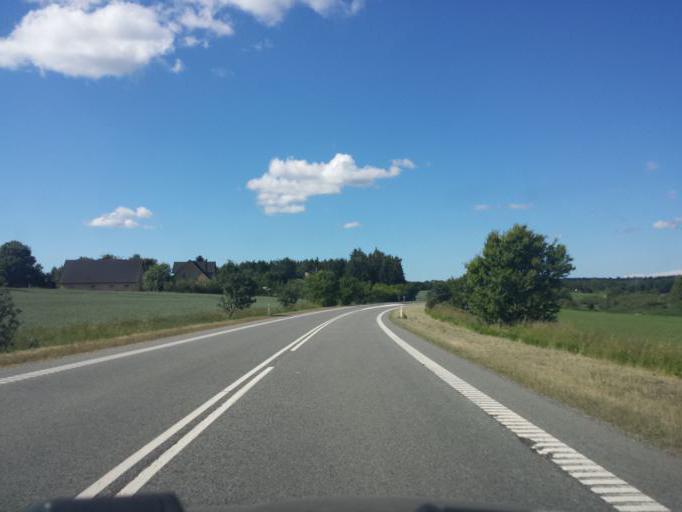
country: DK
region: Capital Region
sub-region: Egedal Kommune
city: Smorumnedre
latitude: 55.7692
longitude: 12.2932
